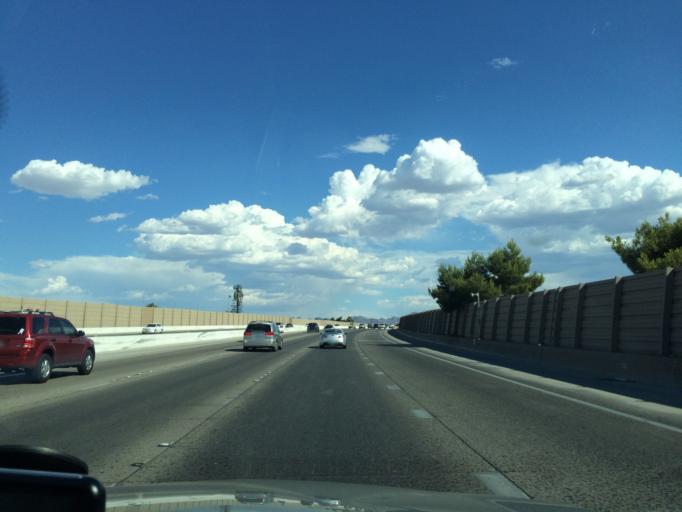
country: US
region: Nevada
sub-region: Clark County
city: Winchester
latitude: 36.1245
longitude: -115.0853
